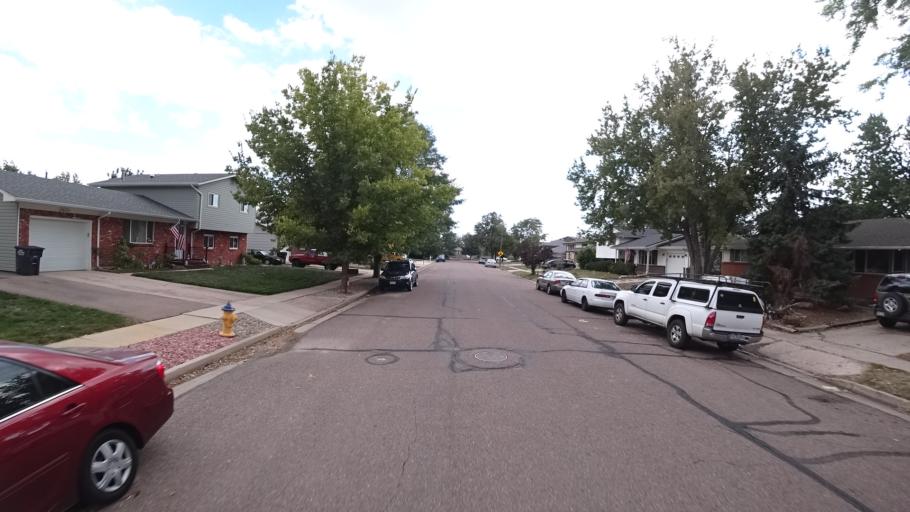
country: US
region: Colorado
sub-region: El Paso County
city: Cimarron Hills
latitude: 38.8482
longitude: -104.7451
